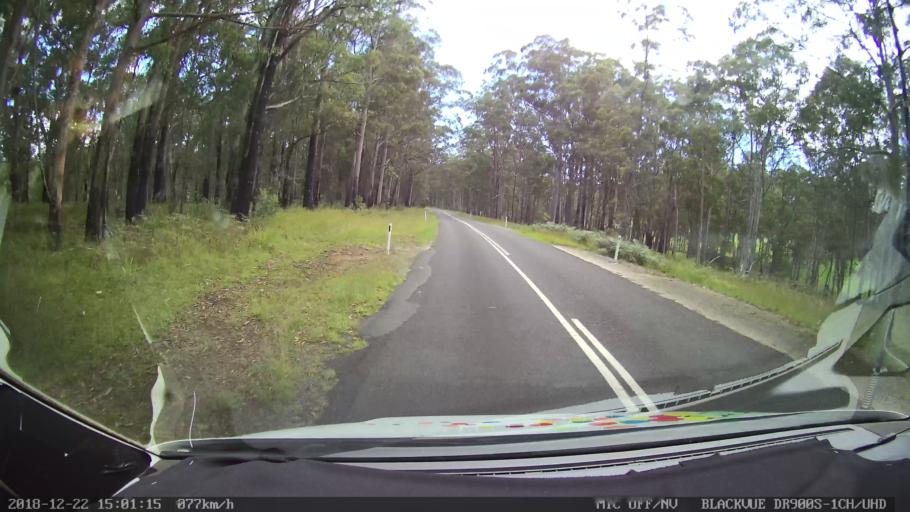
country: AU
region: New South Wales
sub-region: Bellingen
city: Dorrigo
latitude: -30.2526
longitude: 152.4601
